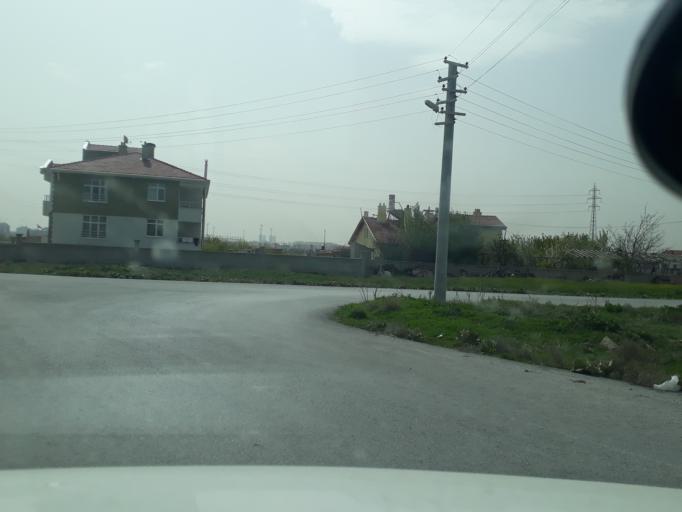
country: TR
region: Konya
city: Sille
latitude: 37.9478
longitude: 32.4755
